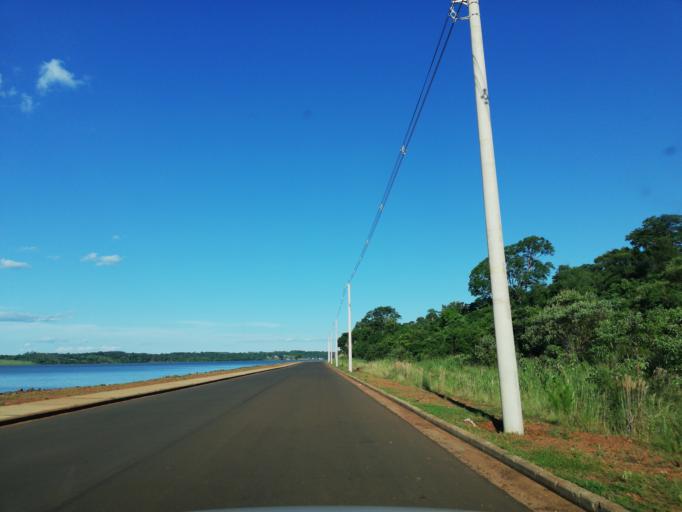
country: AR
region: Misiones
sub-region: Departamento de Candelaria
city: Candelaria
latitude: -27.4508
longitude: -55.7795
